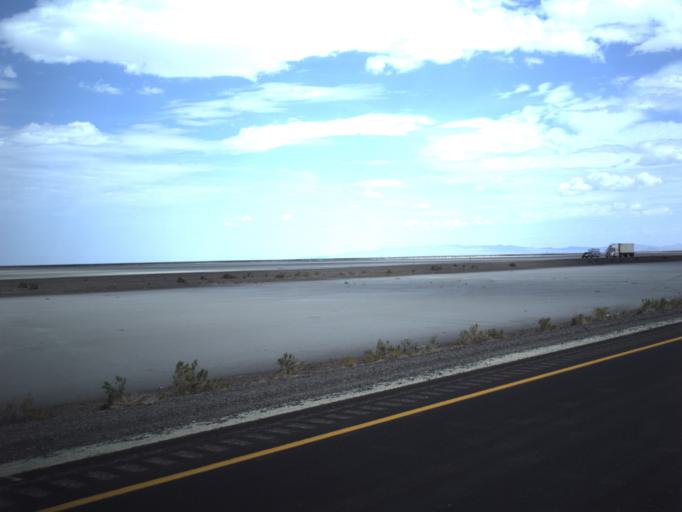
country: US
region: Utah
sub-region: Tooele County
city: Wendover
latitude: 40.7323
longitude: -113.5608
